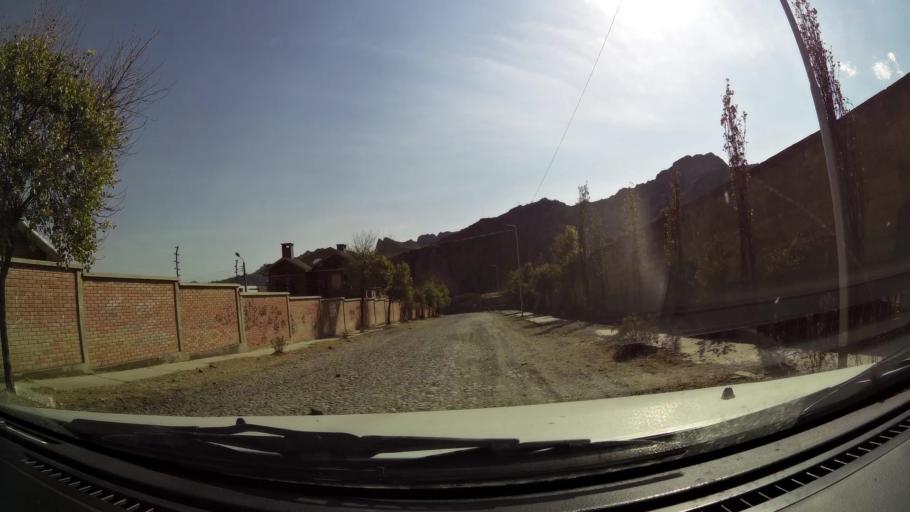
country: BO
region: La Paz
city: La Paz
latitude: -16.5090
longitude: -68.0532
